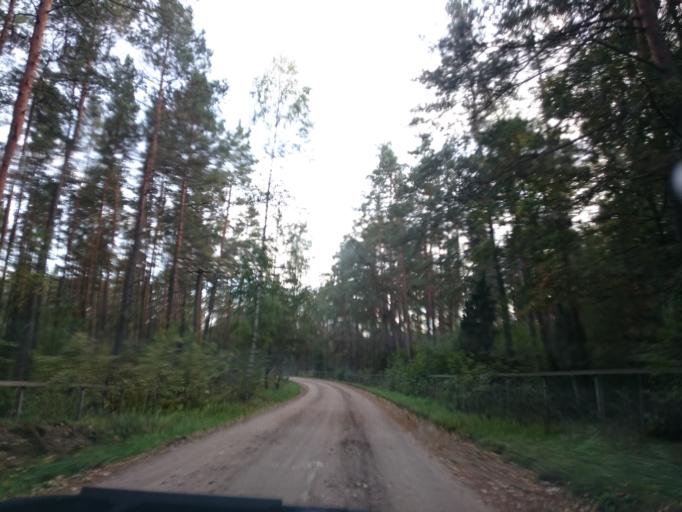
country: LV
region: Garkalne
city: Garkalne
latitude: 57.0465
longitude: 24.3839
